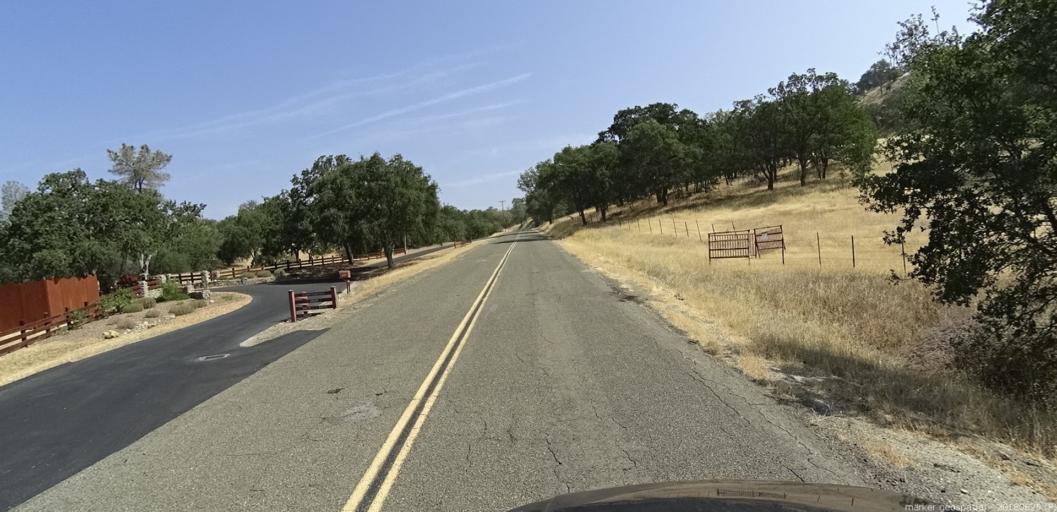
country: US
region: California
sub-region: San Luis Obispo County
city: San Miguel
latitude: 35.9154
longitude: -120.5350
